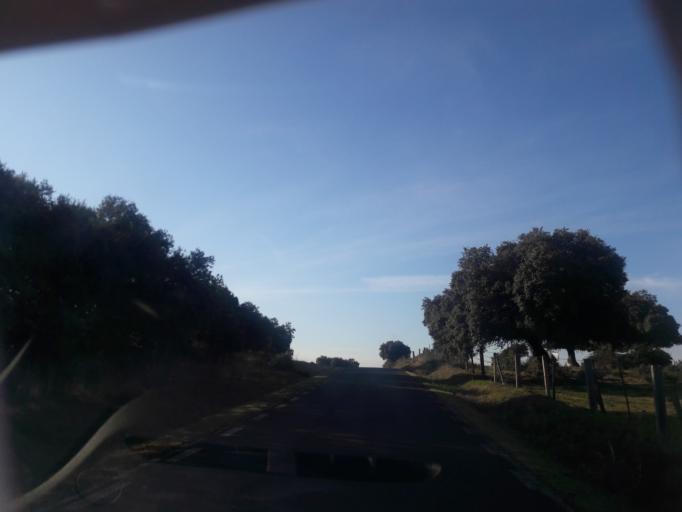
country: ES
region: Castille and Leon
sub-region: Provincia de Salamanca
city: Montejo
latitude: 40.6189
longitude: -5.6082
